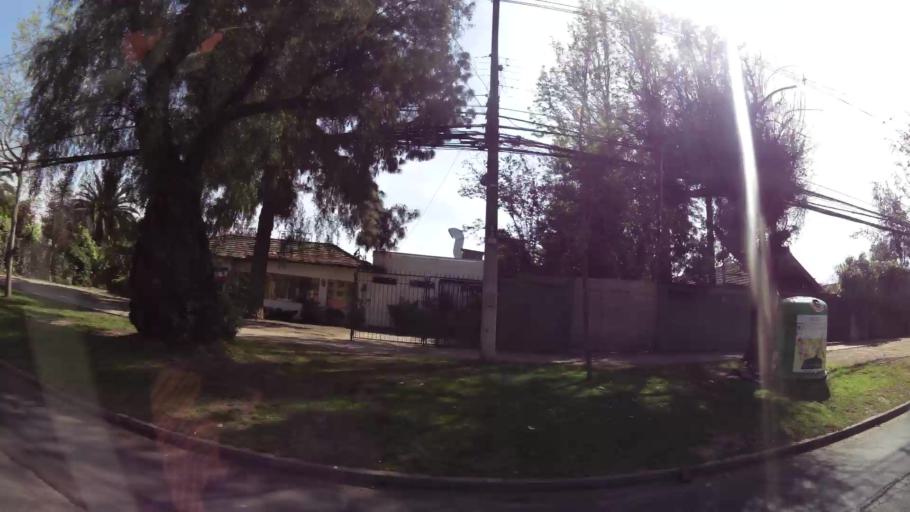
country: CL
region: Santiago Metropolitan
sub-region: Provincia de Santiago
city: Villa Presidente Frei, Nunoa, Santiago, Chile
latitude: -33.5223
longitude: -70.5645
